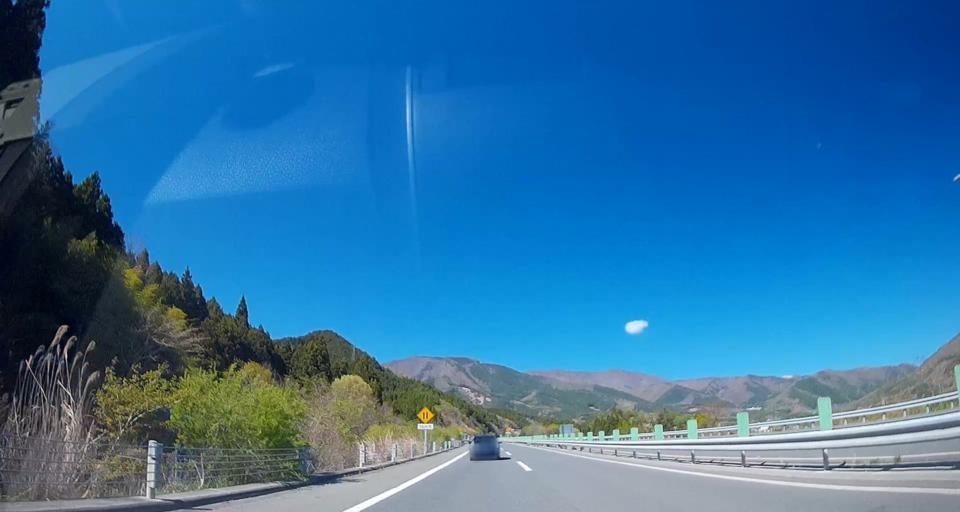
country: JP
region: Iwate
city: Ofunato
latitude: 39.1095
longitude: 141.7096
